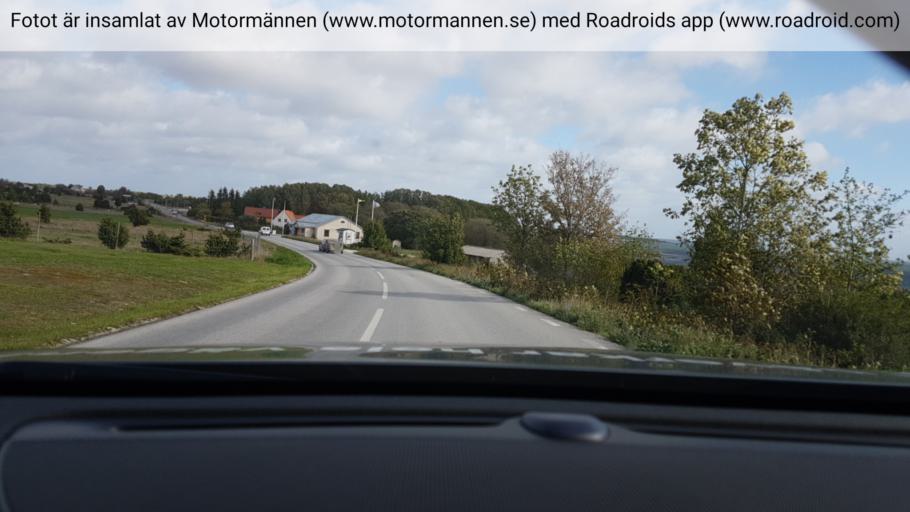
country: SE
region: Gotland
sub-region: Gotland
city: Slite
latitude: 57.9153
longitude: 19.1339
